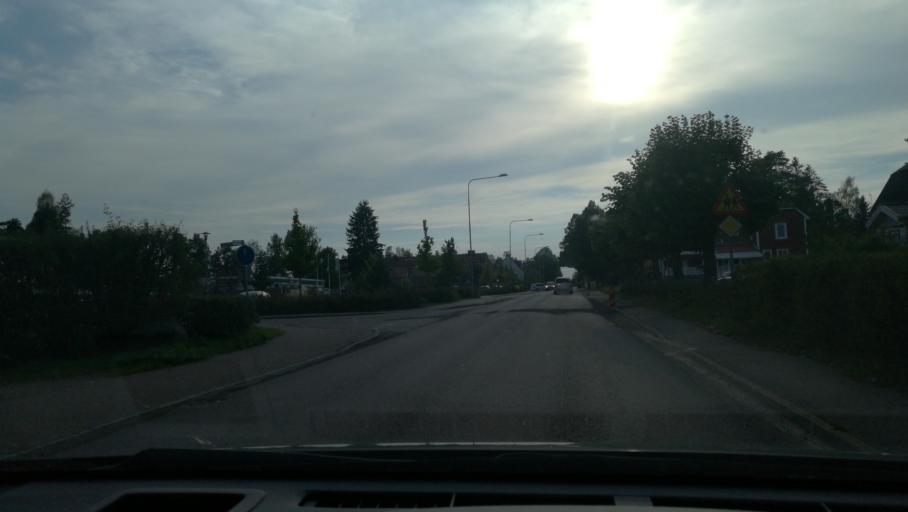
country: SE
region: Dalarna
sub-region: Avesta Kommun
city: Avesta
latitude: 60.1592
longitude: 16.1825
